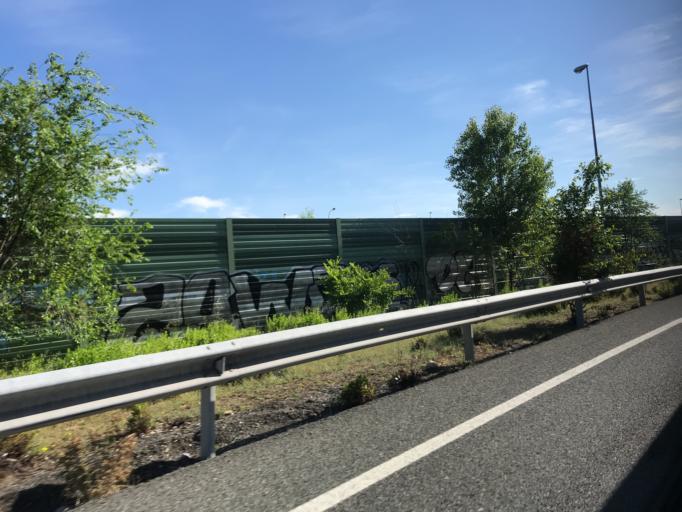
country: ES
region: Madrid
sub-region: Provincia de Madrid
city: San Blas
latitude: 40.4138
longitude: -3.6231
